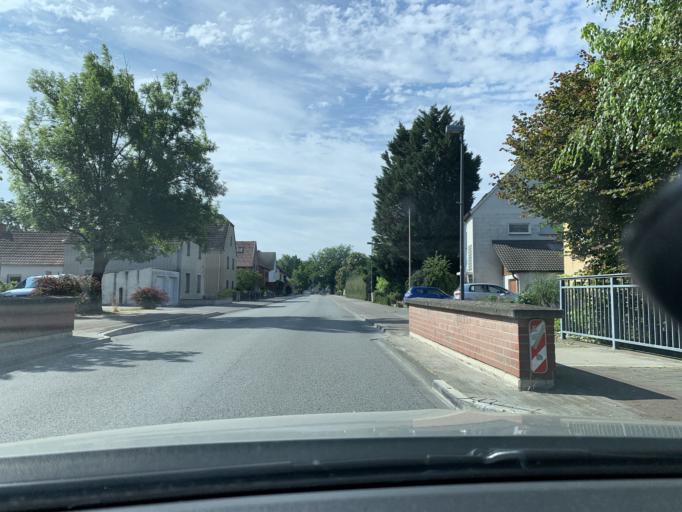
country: DE
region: North Rhine-Westphalia
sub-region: Regierungsbezirk Arnsberg
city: Lippstadt
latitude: 51.6991
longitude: 8.3745
